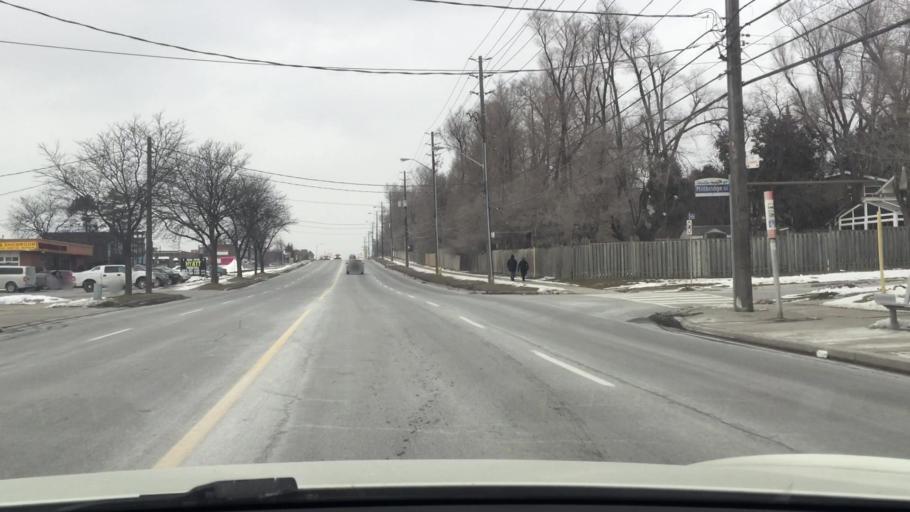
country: CA
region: Ontario
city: Scarborough
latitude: 43.7624
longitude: -79.2692
